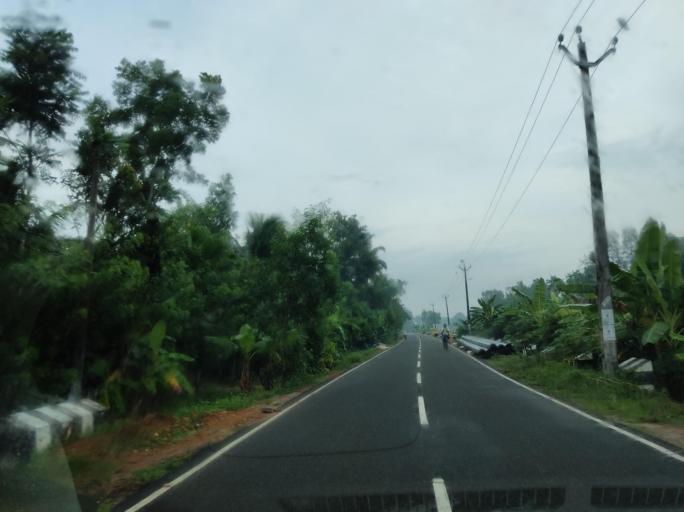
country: IN
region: Kerala
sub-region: Alappuzha
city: Alleppey
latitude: 9.5793
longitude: 76.3318
